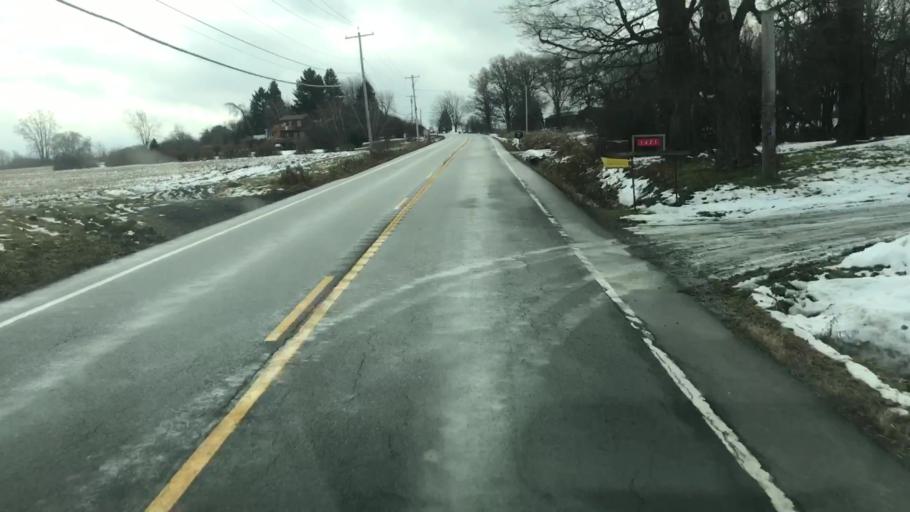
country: US
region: New York
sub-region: Onondaga County
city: Skaneateles
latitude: 42.8500
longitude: -76.3926
